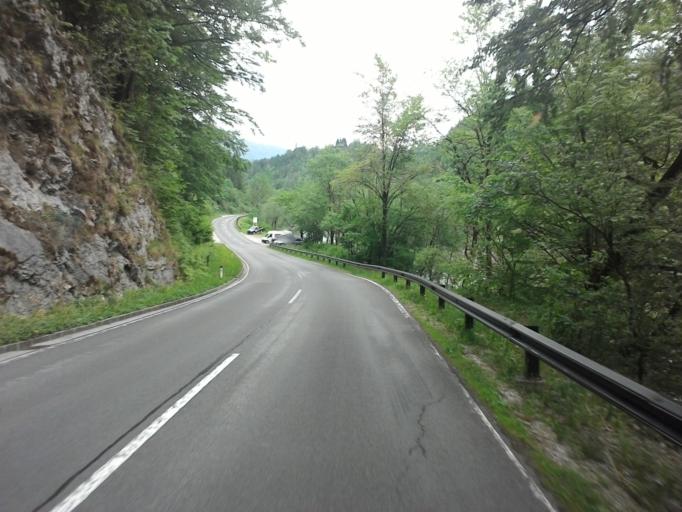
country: AT
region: Styria
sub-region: Politischer Bezirk Leoben
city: Hieflau
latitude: 47.6324
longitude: 14.7592
